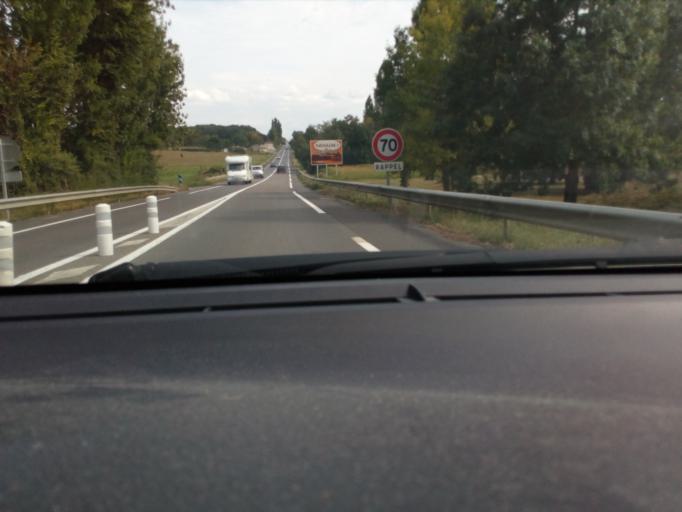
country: FR
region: Poitou-Charentes
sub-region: Departement de la Charente
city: Fleac
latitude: 45.6764
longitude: 0.0873
